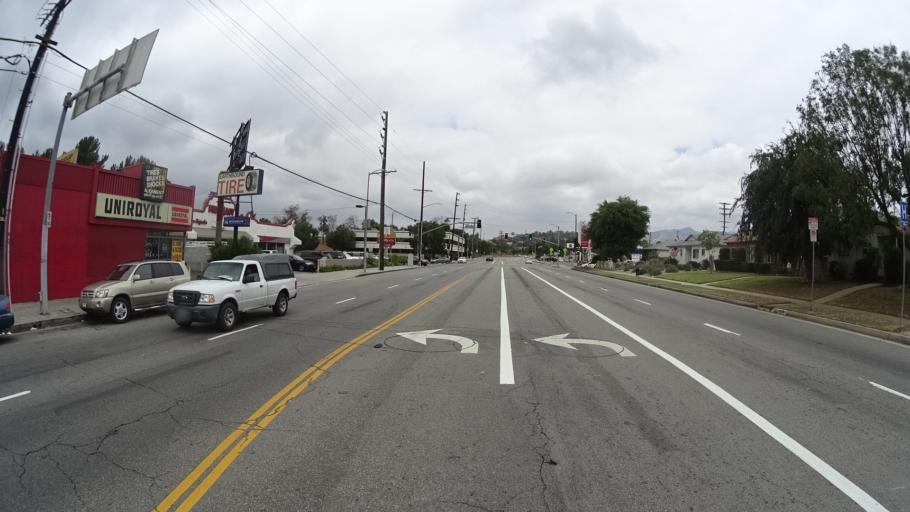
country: US
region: California
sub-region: Los Angeles County
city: San Fernando
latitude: 34.2793
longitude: -118.4540
